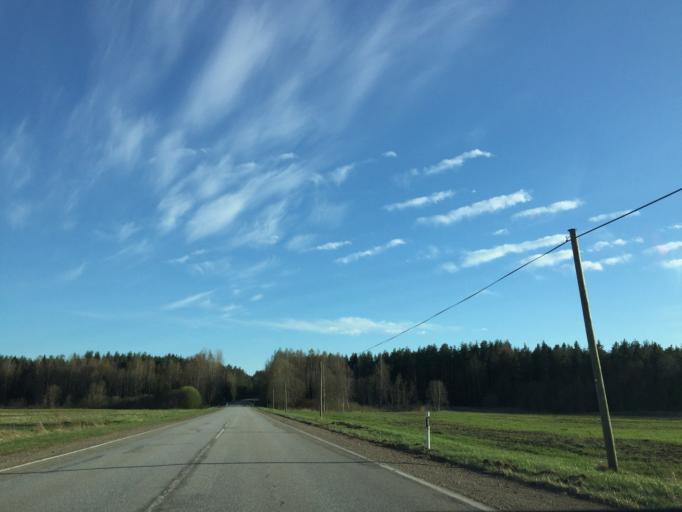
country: LV
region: Valkas Rajons
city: Valka
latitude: 57.7406
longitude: 25.9458
